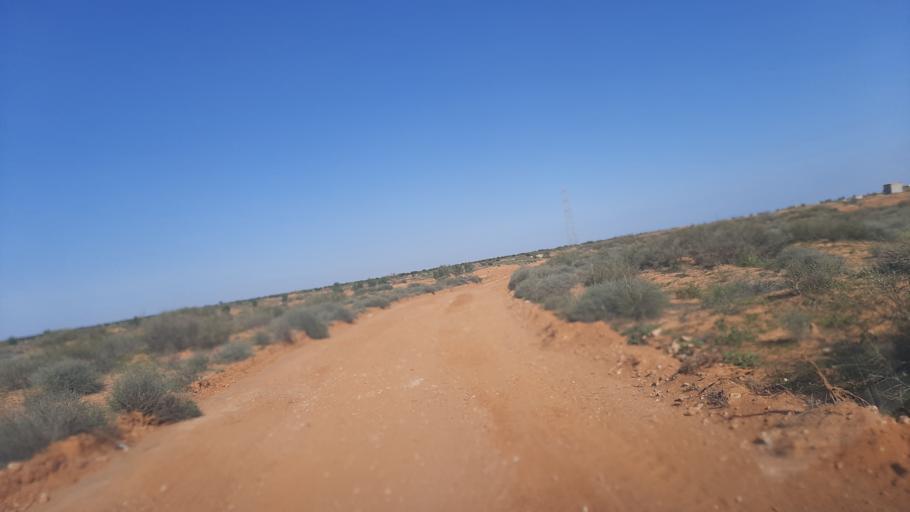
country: TN
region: Madanin
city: Medenine
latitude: 33.2762
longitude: 10.7722
